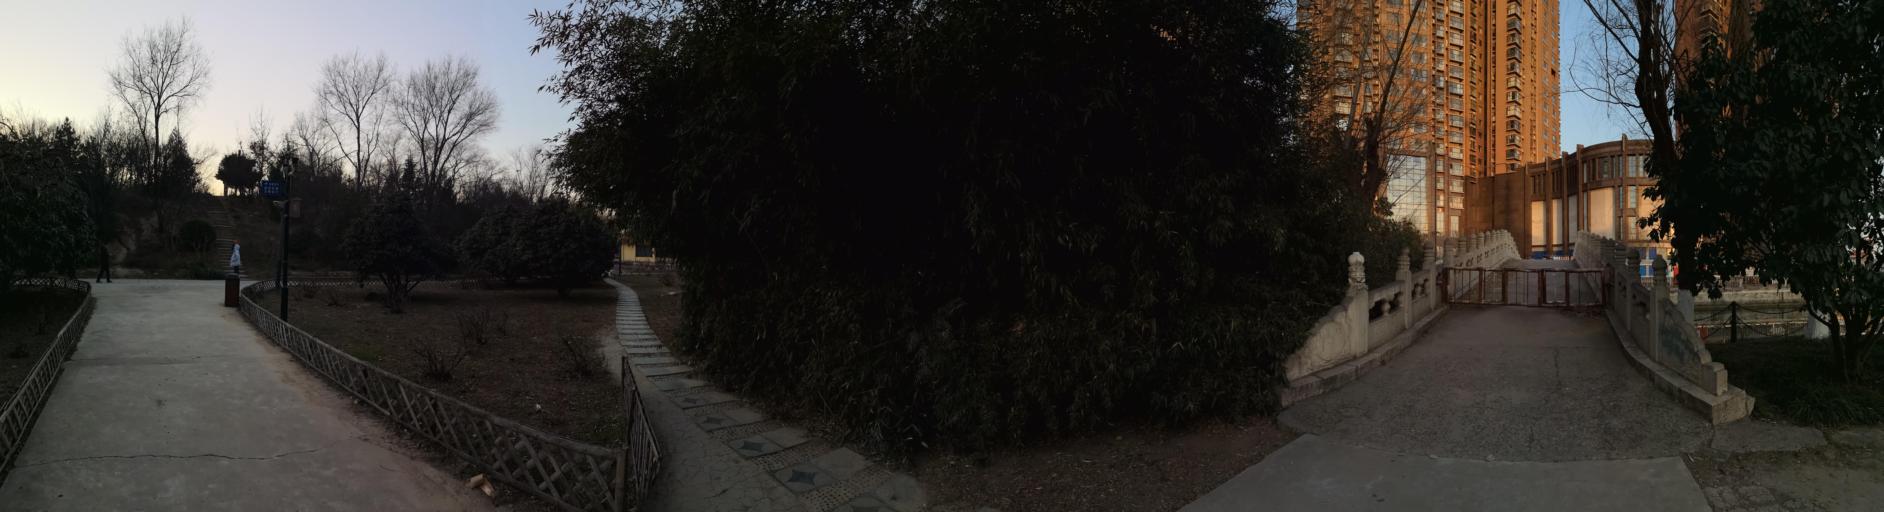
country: CN
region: Henan Sheng
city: Zhongyuanlu
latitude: 35.7736
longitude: 115.0789
